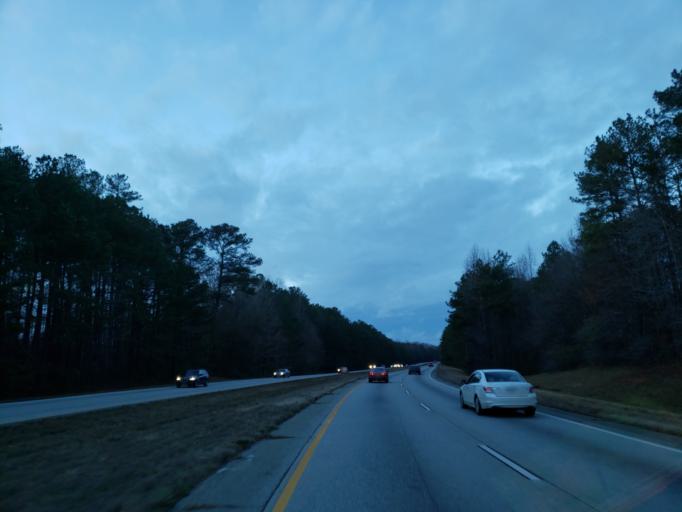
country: US
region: Georgia
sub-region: Fulton County
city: Union City
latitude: 33.6877
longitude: -84.5727
